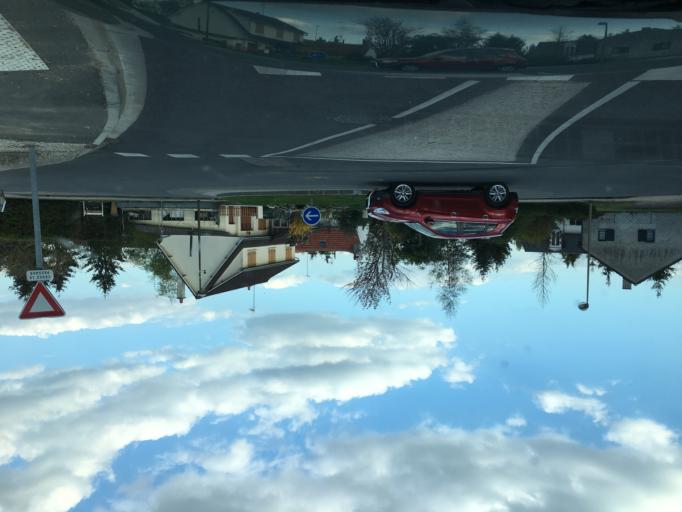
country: FR
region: Centre
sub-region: Departement du Loiret
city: Saint-Denis-en-Val
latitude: 47.8724
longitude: 1.9599
